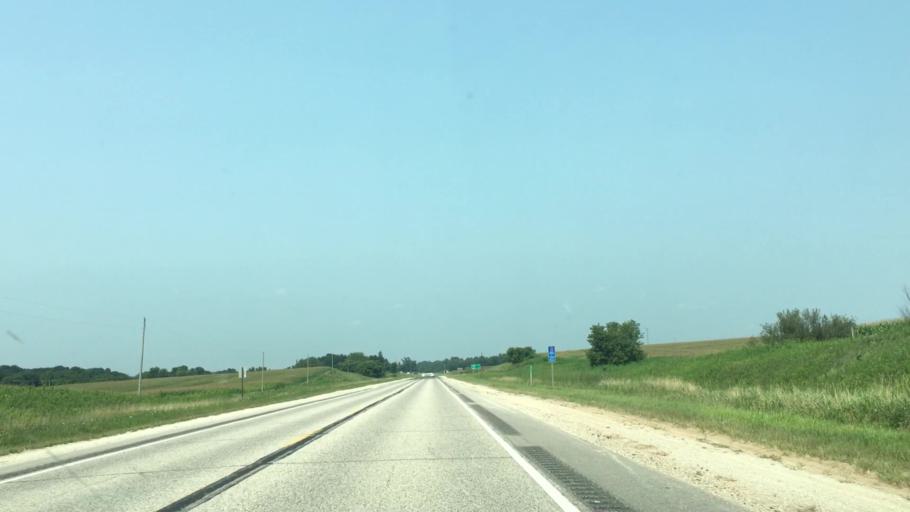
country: US
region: Iowa
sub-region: Fayette County
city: Fayette
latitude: 42.8142
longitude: -91.8051
